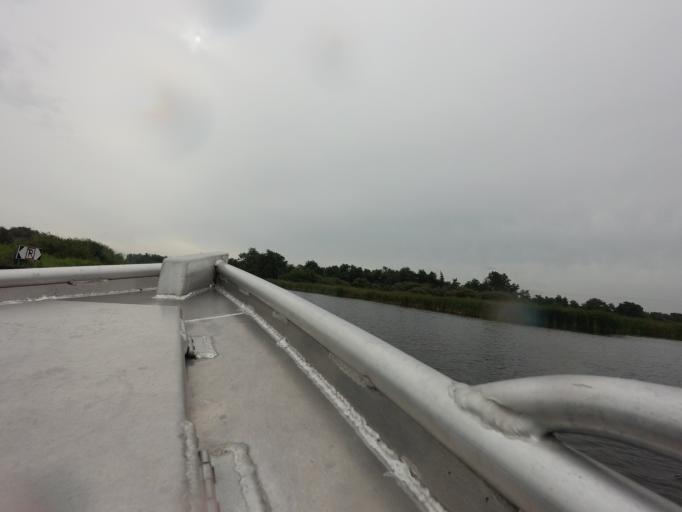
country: NL
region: Overijssel
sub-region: Gemeente Steenwijkerland
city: Sint Jansklooster
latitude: 52.7129
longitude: 6.0169
